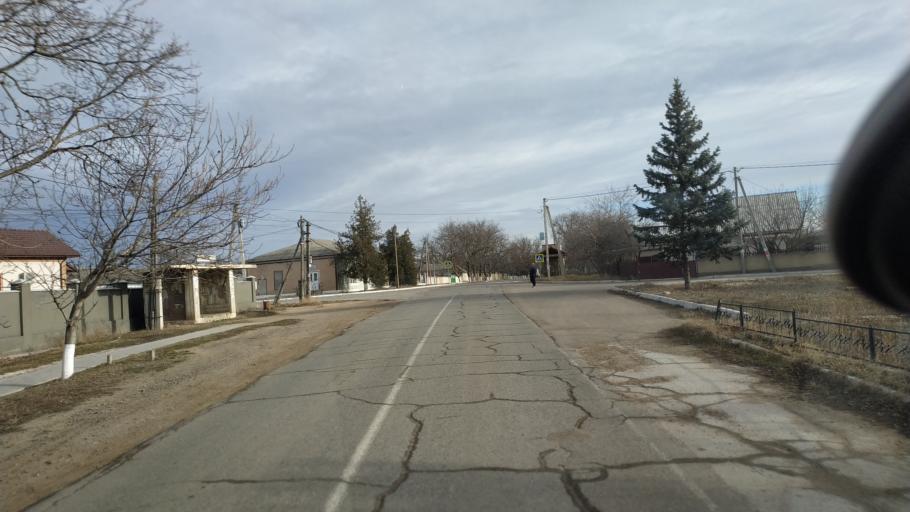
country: MD
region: Criuleni
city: Criuleni
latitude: 47.1643
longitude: 29.1210
